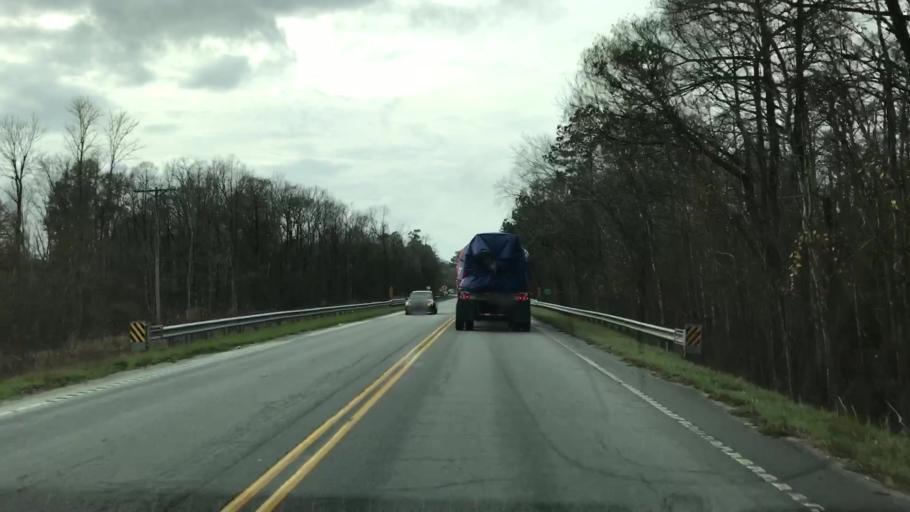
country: US
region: South Carolina
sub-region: Berkeley County
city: Bonneau Beach
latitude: 33.2690
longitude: -79.9053
